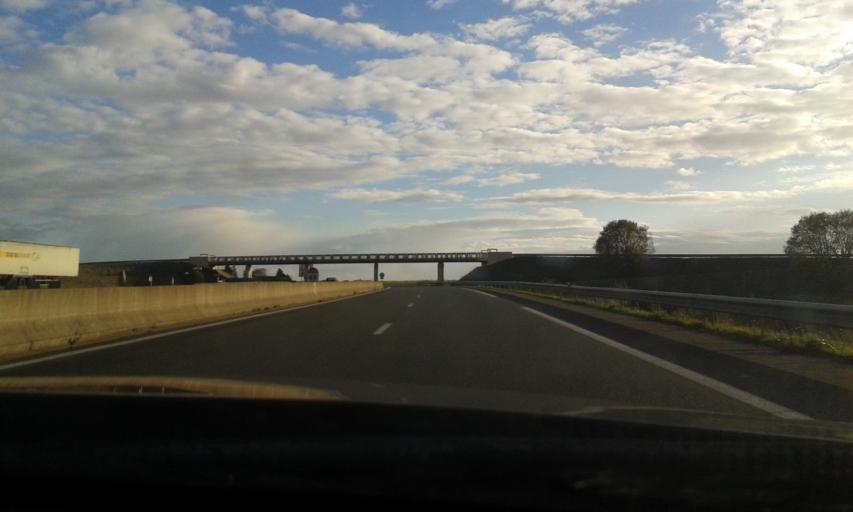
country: FR
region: Centre
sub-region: Departement d'Eure-et-Loir
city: Villemeux-sur-Eure
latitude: 48.5981
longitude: 1.4230
